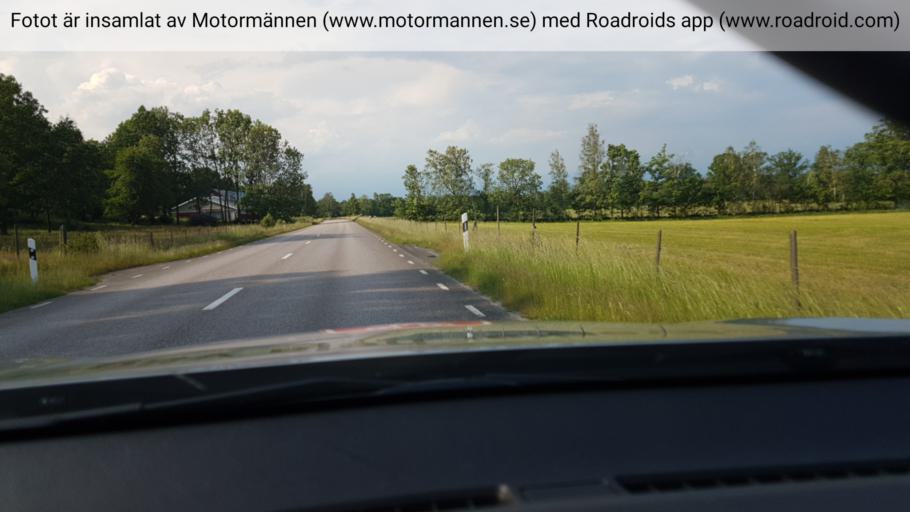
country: SE
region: Vaestra Goetaland
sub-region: Hjo Kommun
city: Hjo
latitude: 58.1461
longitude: 14.2156
